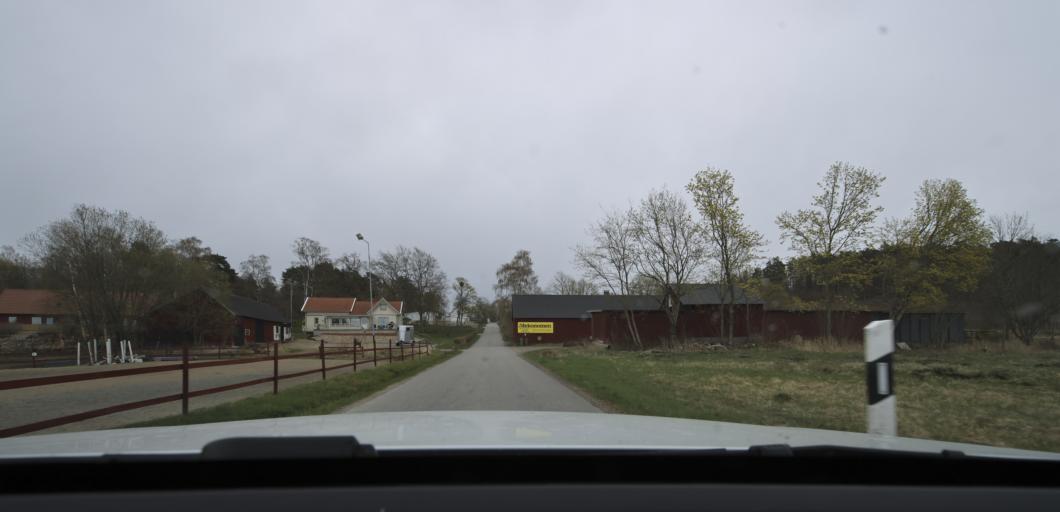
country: SE
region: Halland
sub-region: Varbergs Kommun
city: Tvaaker
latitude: 57.1229
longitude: 12.4535
